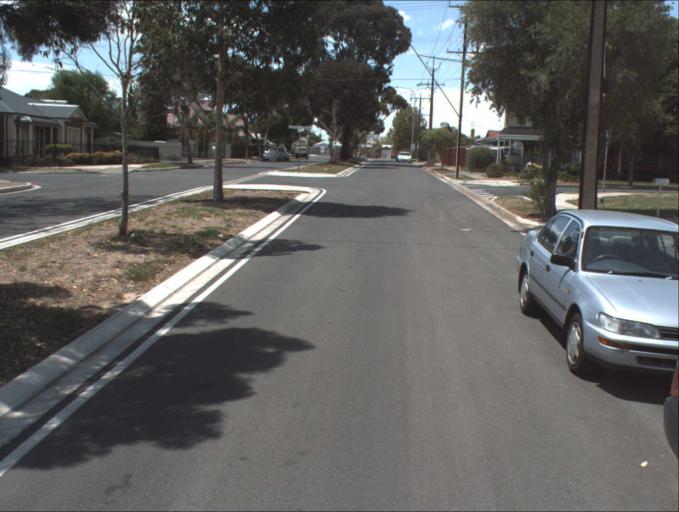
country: AU
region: South Australia
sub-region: Port Adelaide Enfield
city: Enfield
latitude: -34.8504
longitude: 138.6158
